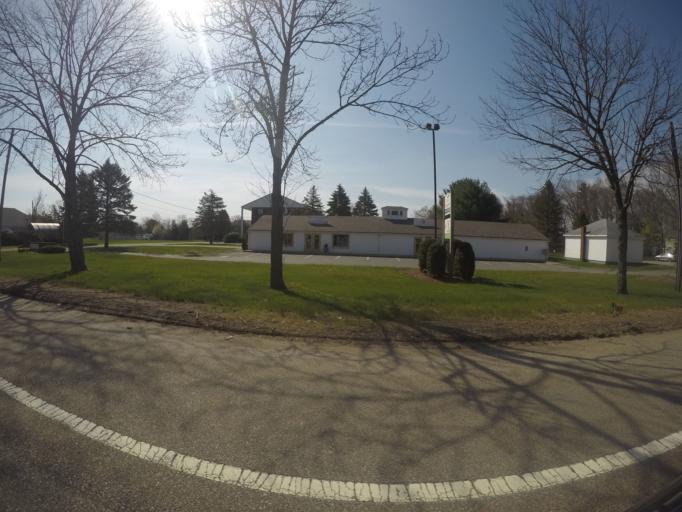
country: US
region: Massachusetts
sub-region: Bristol County
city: Easton
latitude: 42.0515
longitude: -71.0795
